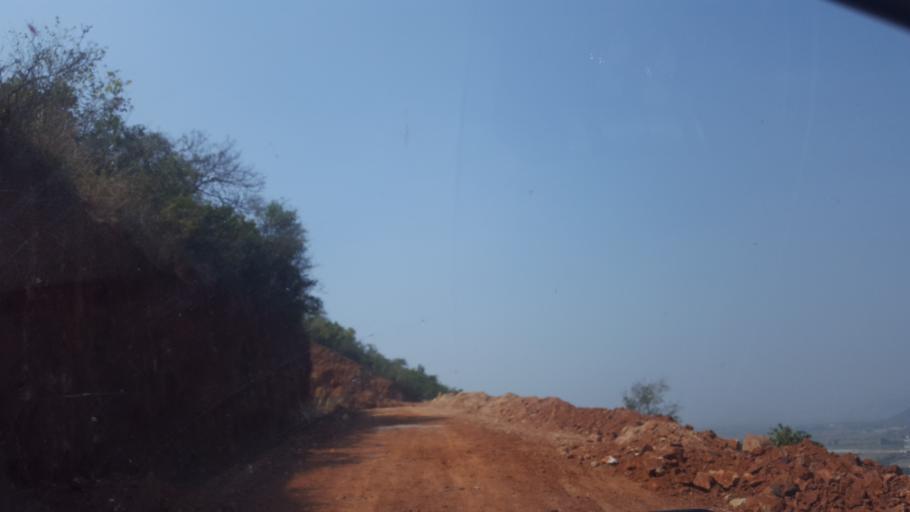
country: IN
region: Andhra Pradesh
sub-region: Srikakulam
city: Palasa
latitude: 18.7198
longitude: 84.3956
